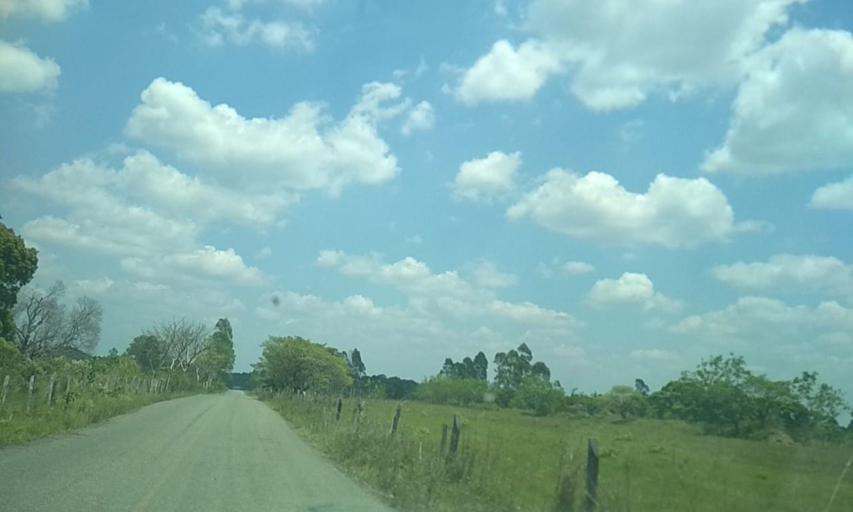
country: MX
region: Tabasco
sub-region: Huimanguillo
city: Francisco Rueda
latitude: 17.7780
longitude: -93.8252
